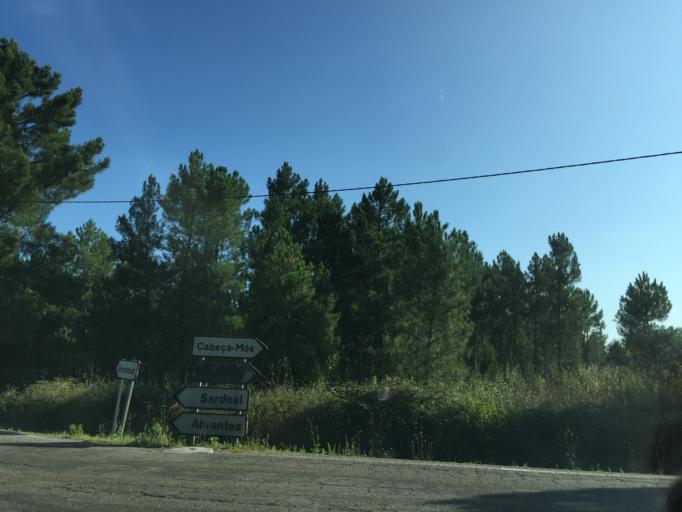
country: PT
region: Santarem
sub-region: Abrantes
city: Alferrarede
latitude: 39.5326
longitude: -8.1369
